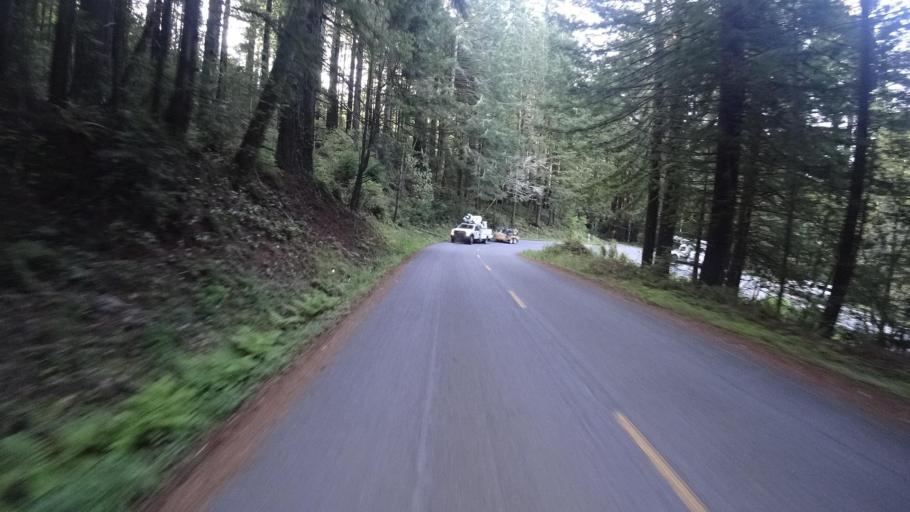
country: US
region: California
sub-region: Humboldt County
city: Bayside
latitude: 40.7551
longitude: -124.0483
